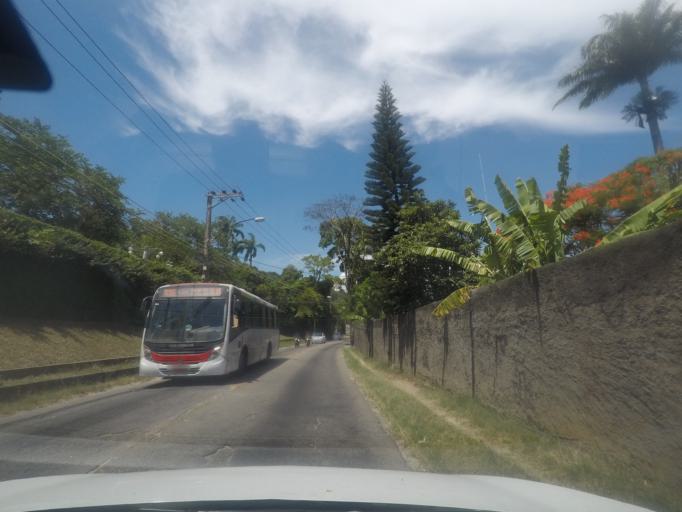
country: BR
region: Rio de Janeiro
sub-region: Itaguai
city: Itaguai
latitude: -23.0003
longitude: -43.6447
